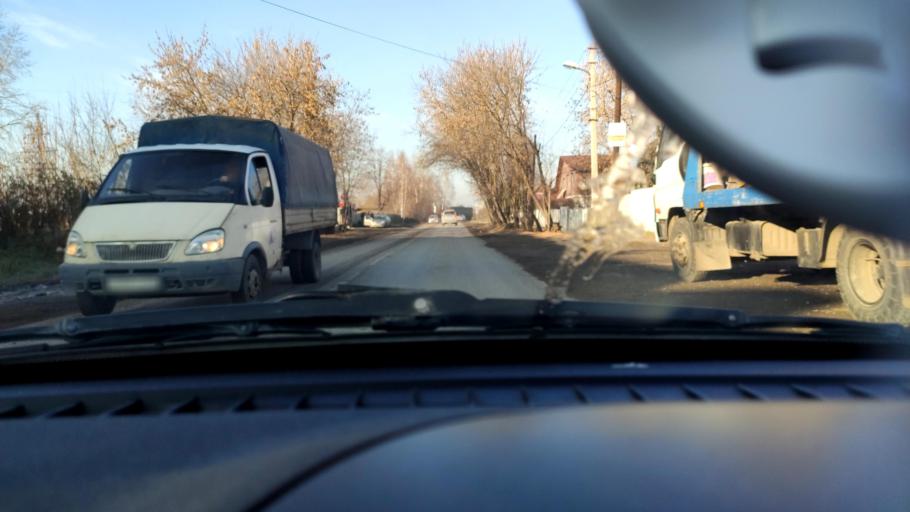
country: RU
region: Perm
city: Perm
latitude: 58.0102
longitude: 56.3215
